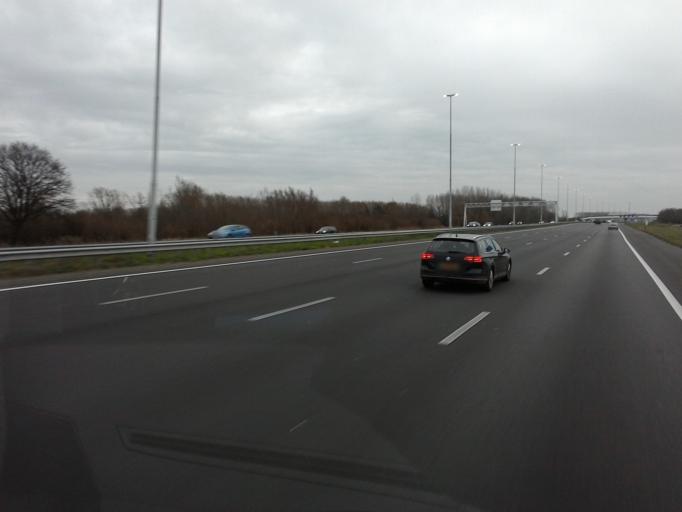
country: NL
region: Gelderland
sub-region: Gemeente Culemborg
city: Culemborg
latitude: 51.9230
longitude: 5.1703
